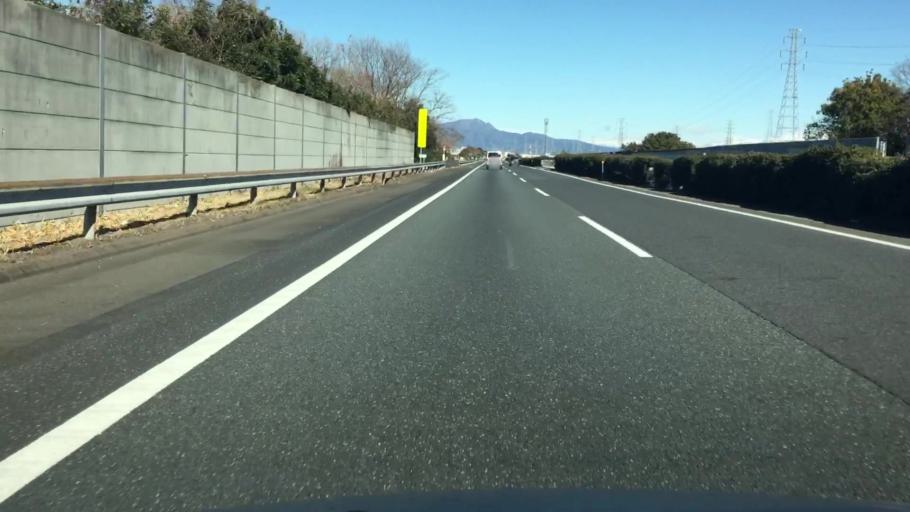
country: JP
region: Gunma
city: Maebashi-shi
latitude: 36.3888
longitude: 139.0259
